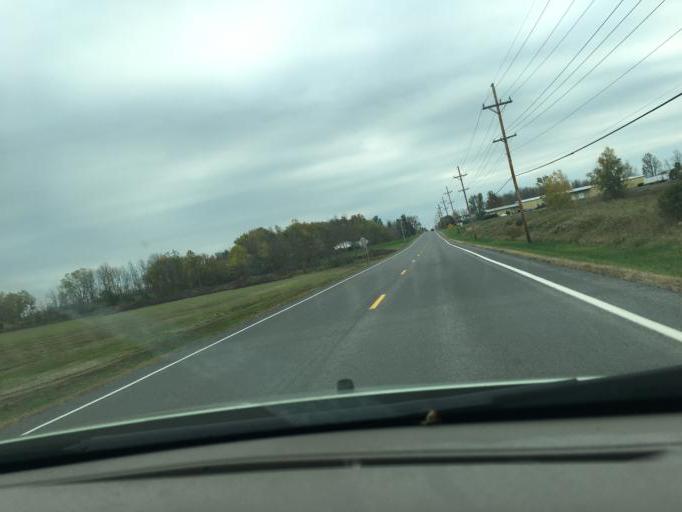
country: US
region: New York
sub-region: Ontario County
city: Manchester
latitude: 42.9710
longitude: -77.3190
